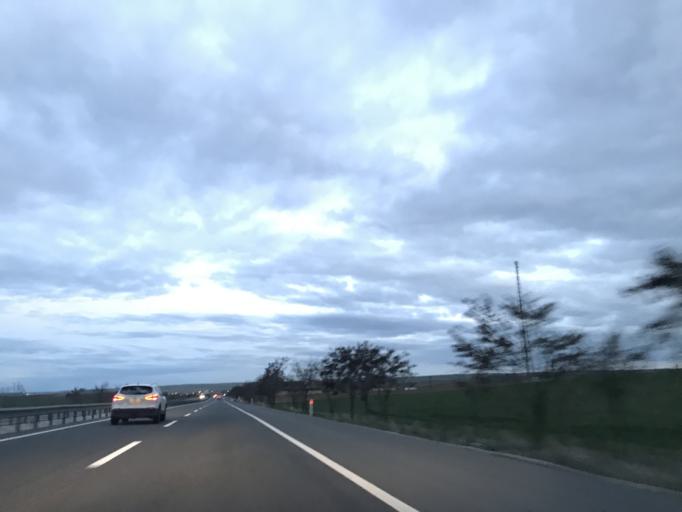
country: TR
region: Konya
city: Kulu
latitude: 39.2454
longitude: 33.0099
